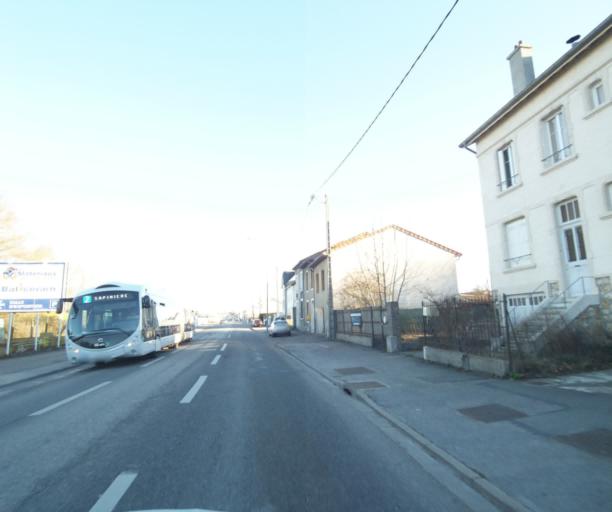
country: FR
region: Lorraine
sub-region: Departement de Meurthe-et-Moselle
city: Heillecourt
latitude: 48.6633
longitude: 6.2193
